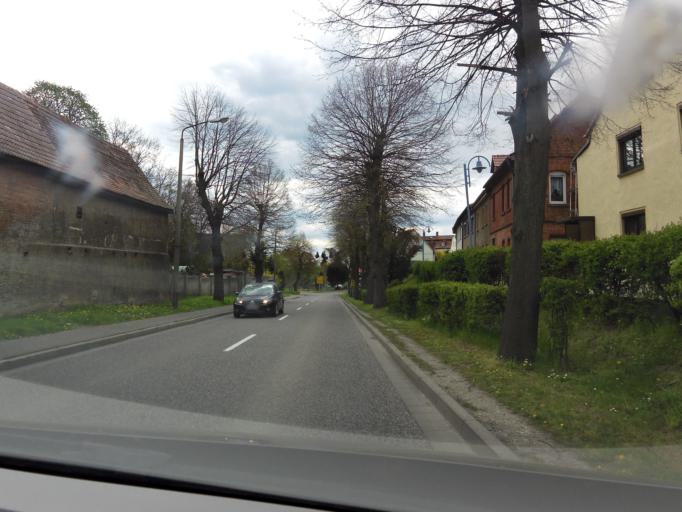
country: DE
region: Saxony-Anhalt
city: Eckartsberga
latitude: 51.1220
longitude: 11.5557
